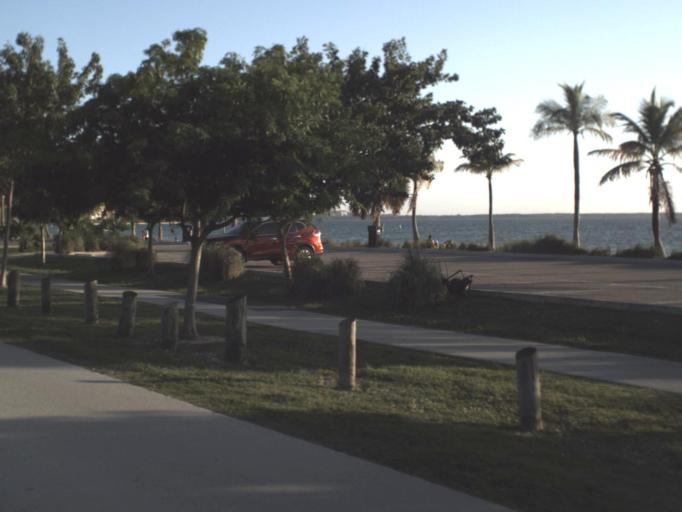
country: US
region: Florida
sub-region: Miami-Dade County
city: Miami
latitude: 25.7399
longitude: -80.1695
